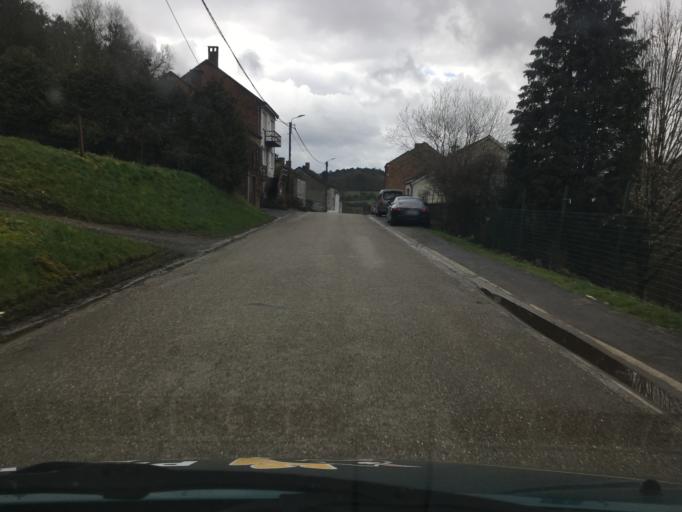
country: FR
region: Champagne-Ardenne
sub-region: Departement des Ardennes
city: Vireux-Molhain
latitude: 50.1002
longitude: 4.6982
